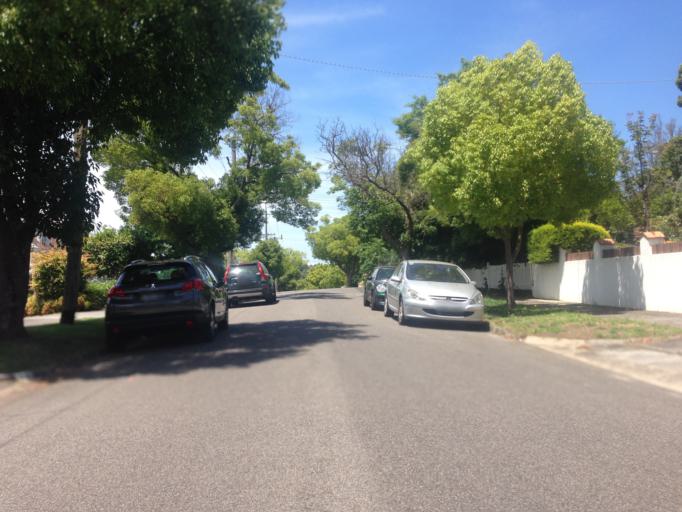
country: AU
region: Victoria
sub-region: Boroondara
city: Kew East
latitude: -37.7901
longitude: 145.0663
